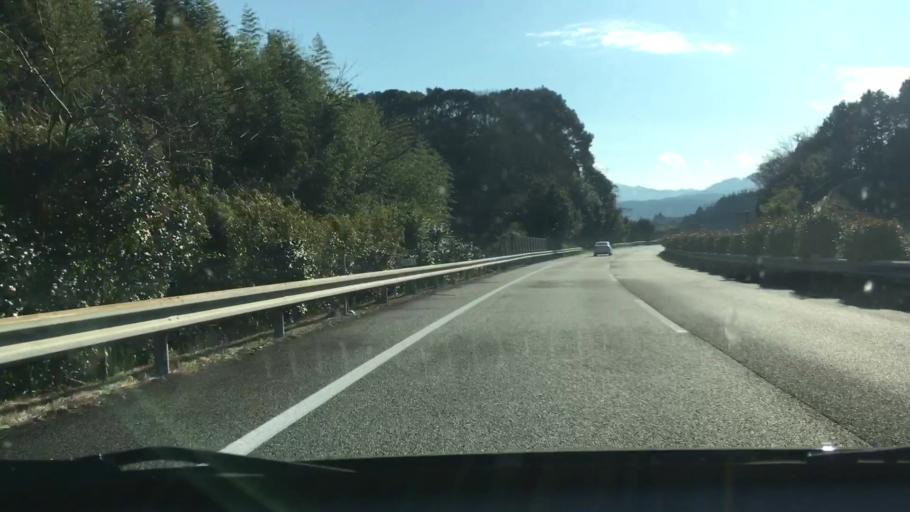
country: JP
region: Kumamoto
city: Hitoyoshi
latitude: 32.2171
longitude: 130.7798
